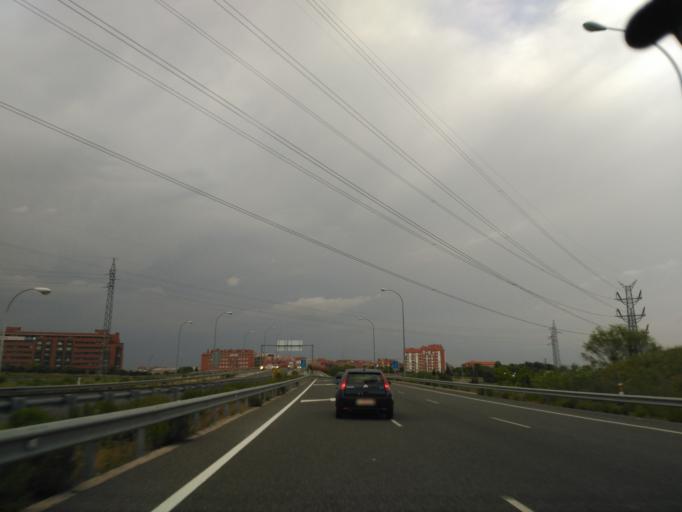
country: ES
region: Madrid
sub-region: Provincia de Madrid
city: Villaverde
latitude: 40.3374
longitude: -3.6725
